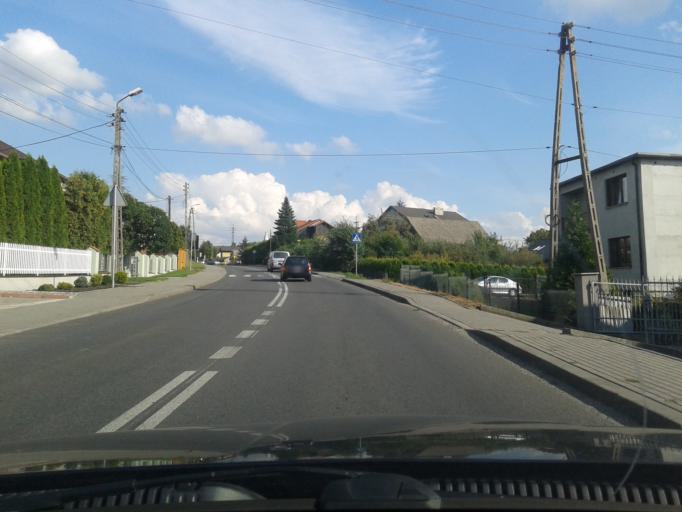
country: PL
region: Silesian Voivodeship
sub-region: Powiat wodzislawski
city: Gorzyce
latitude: 49.9601
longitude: 18.3916
